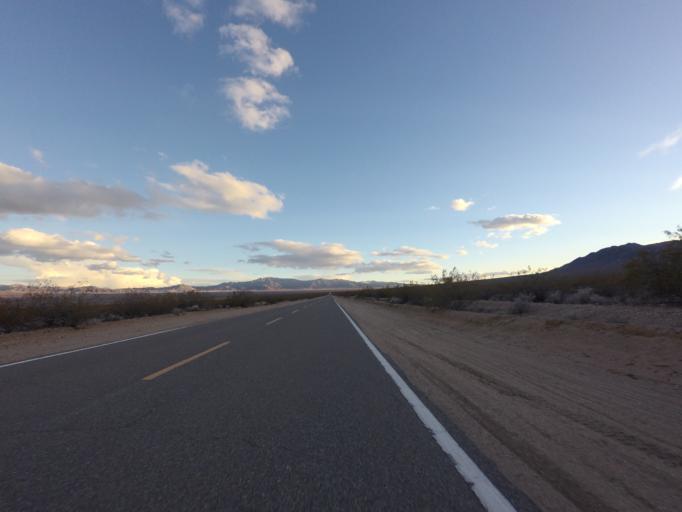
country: US
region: Nevada
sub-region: Clark County
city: Sandy Valley
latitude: 35.4543
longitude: -115.3892
